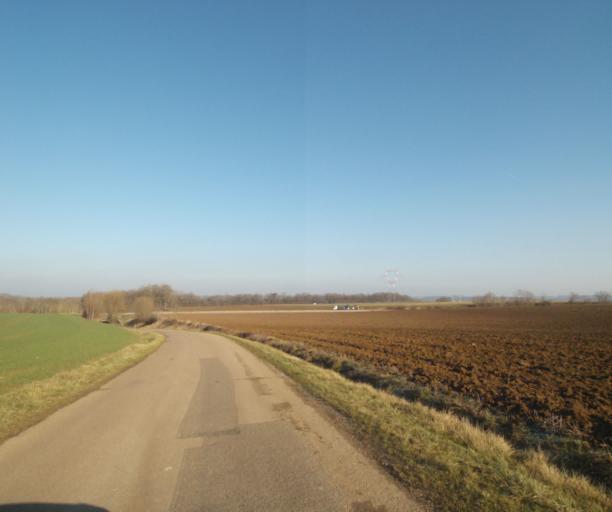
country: FR
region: Champagne-Ardenne
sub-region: Departement de la Haute-Marne
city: Chevillon
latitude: 48.5148
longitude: 5.0895
